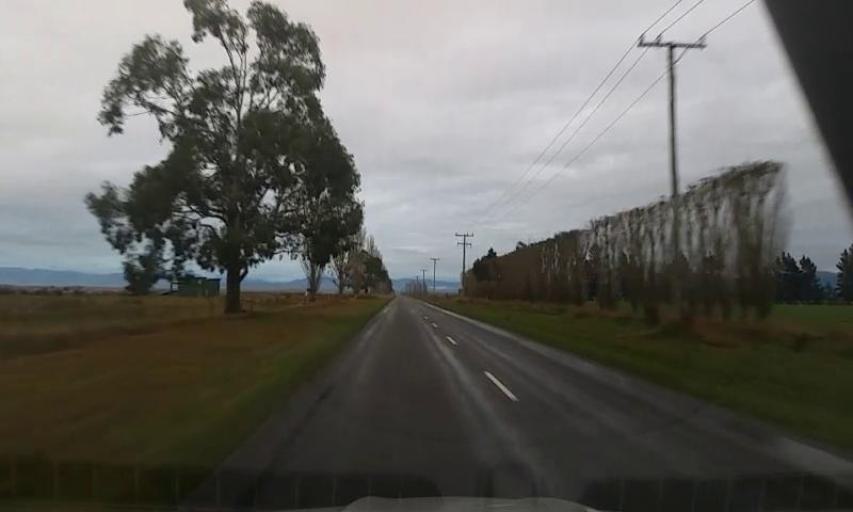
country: NZ
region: Canterbury
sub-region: Ashburton District
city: Methven
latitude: -43.7391
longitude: 171.6764
